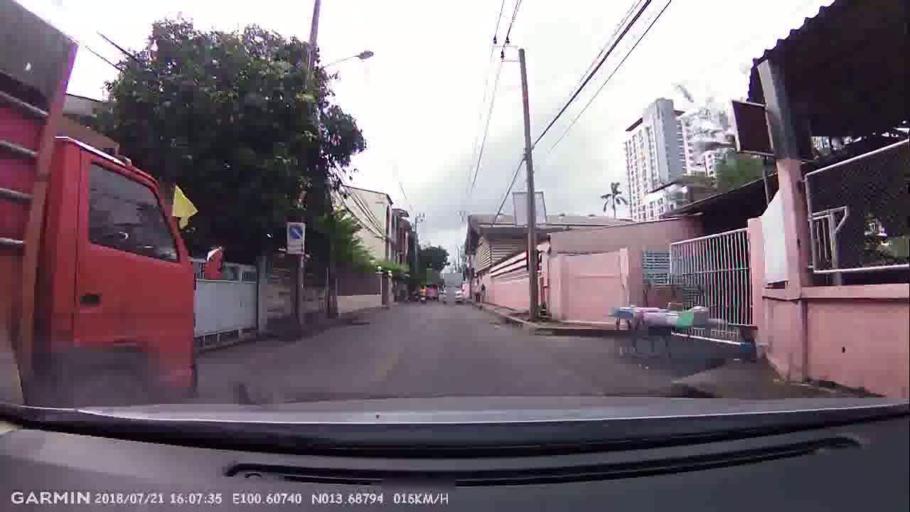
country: TH
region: Bangkok
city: Phra Khanong
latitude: 13.6880
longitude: 100.6074
